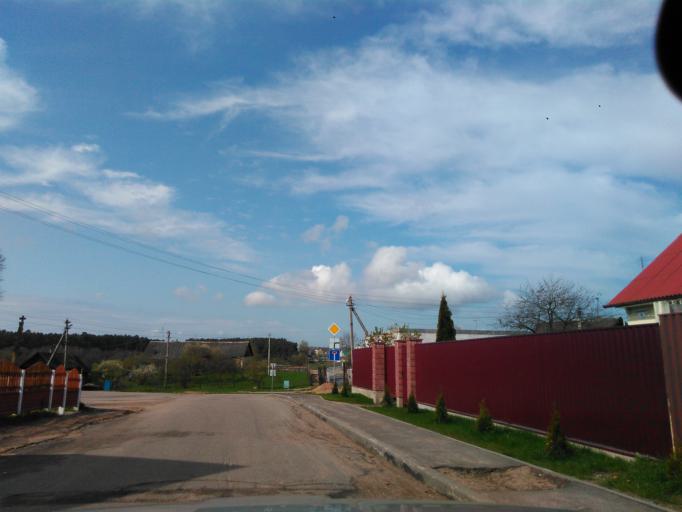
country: BY
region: Minsk
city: Rakaw
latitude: 53.9665
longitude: 27.0557
